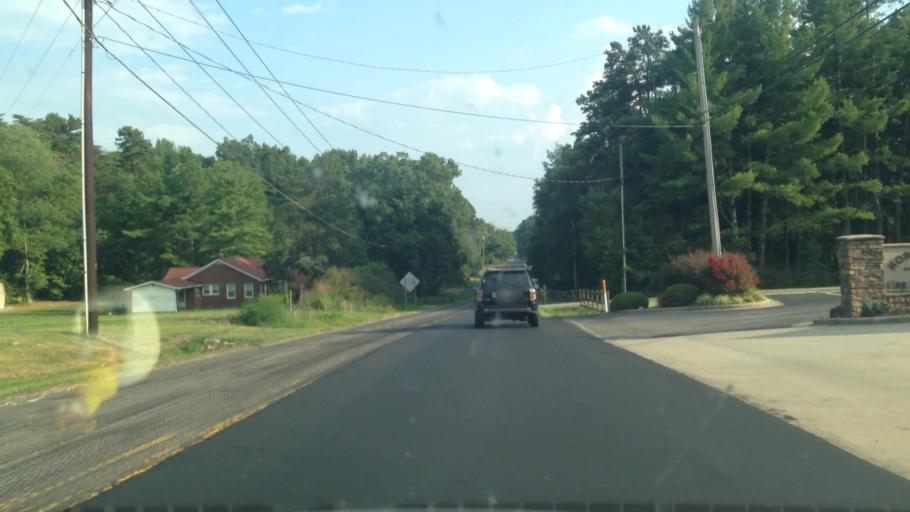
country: US
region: North Carolina
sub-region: Davidson County
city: Wallburg
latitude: 36.0186
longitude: -80.0601
